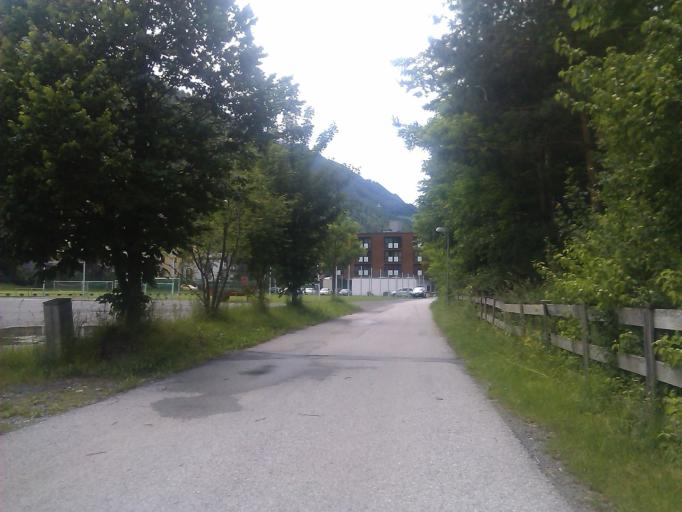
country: AT
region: Tyrol
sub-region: Politischer Bezirk Landeck
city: Ried im Oberinntal
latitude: 47.0600
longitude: 10.6580
